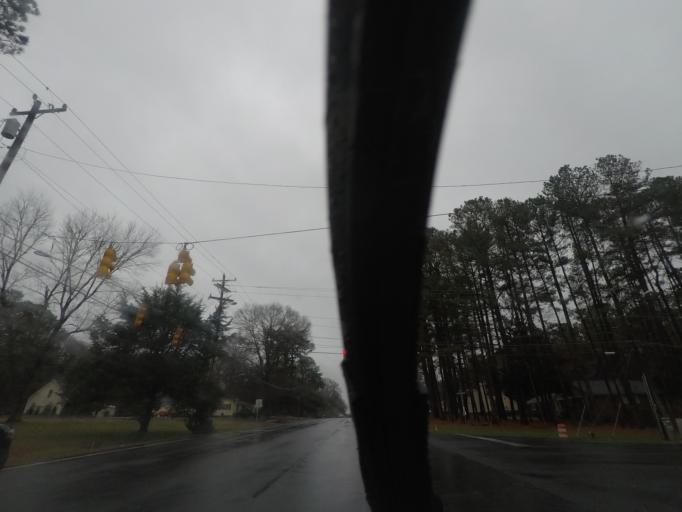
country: US
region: North Carolina
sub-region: Durham County
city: Durham
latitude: 36.0535
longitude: -78.9738
